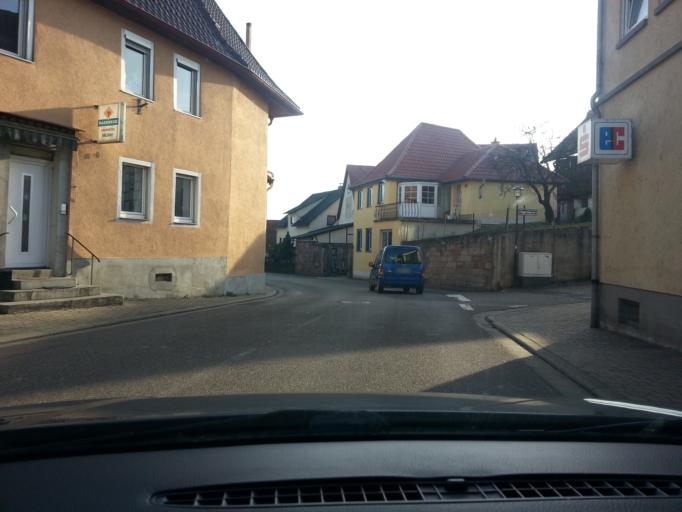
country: DE
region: Rheinland-Pfalz
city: Billigheim-Ingenheim
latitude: 49.1371
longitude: 8.0996
